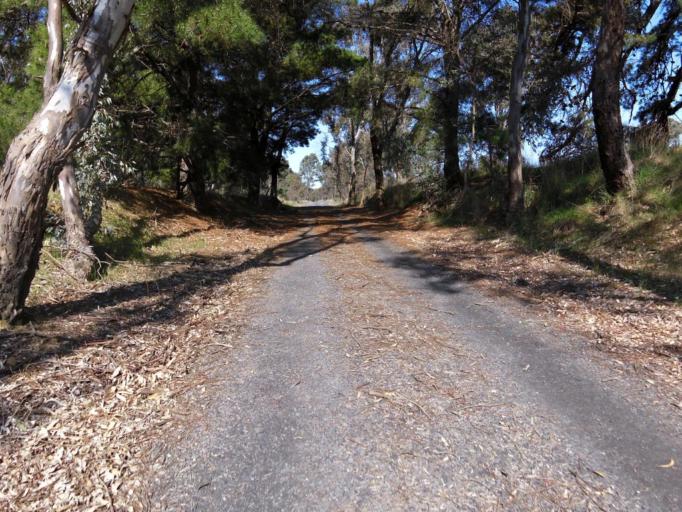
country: AU
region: Victoria
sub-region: Murrindindi
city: Alexandra
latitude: -36.9916
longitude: 145.7378
